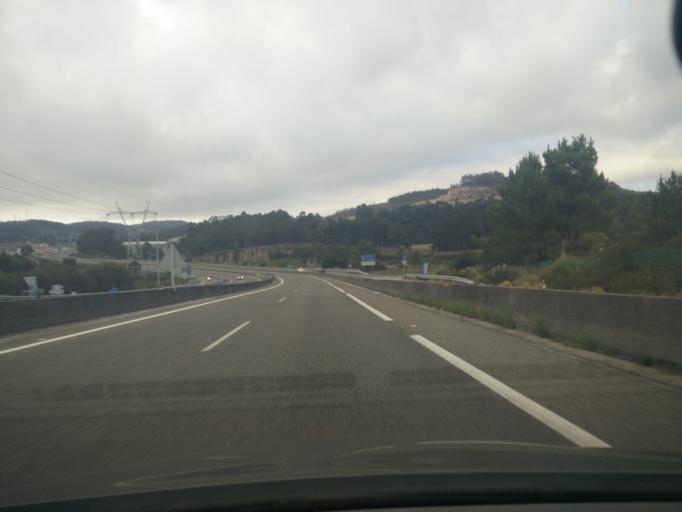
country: ES
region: Galicia
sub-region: Provincia da Coruna
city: Arteixo
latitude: 43.3051
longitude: -8.4751
